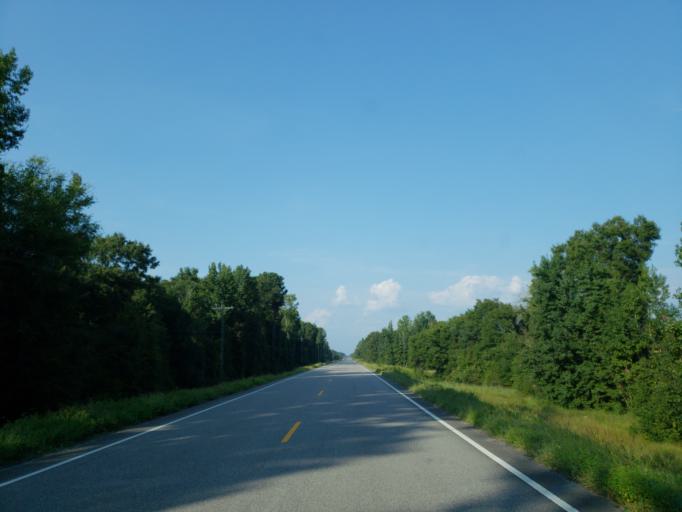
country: US
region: Alabama
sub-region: Sumter County
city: Livingston
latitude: 32.7076
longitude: -88.0837
